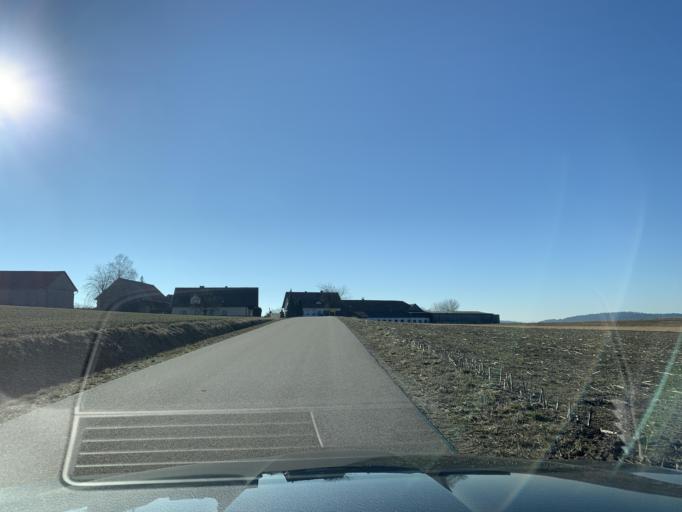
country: DE
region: Bavaria
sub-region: Upper Palatinate
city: Winklarn
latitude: 49.4151
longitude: 12.4503
